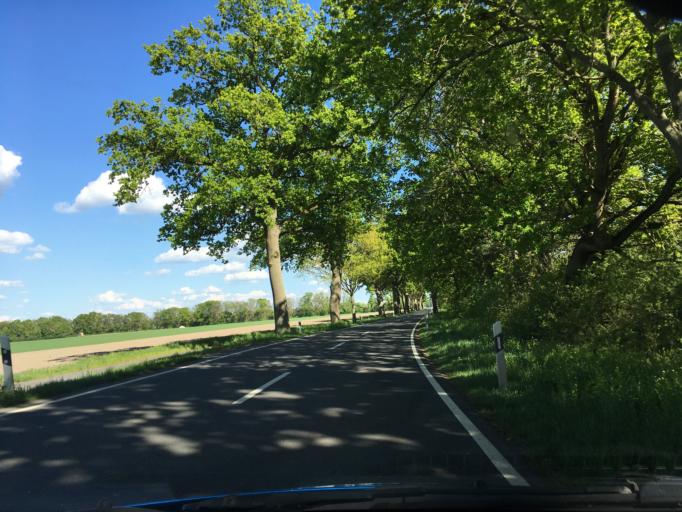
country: DE
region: Lower Saxony
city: Gartow
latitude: 53.0271
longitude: 11.4783
